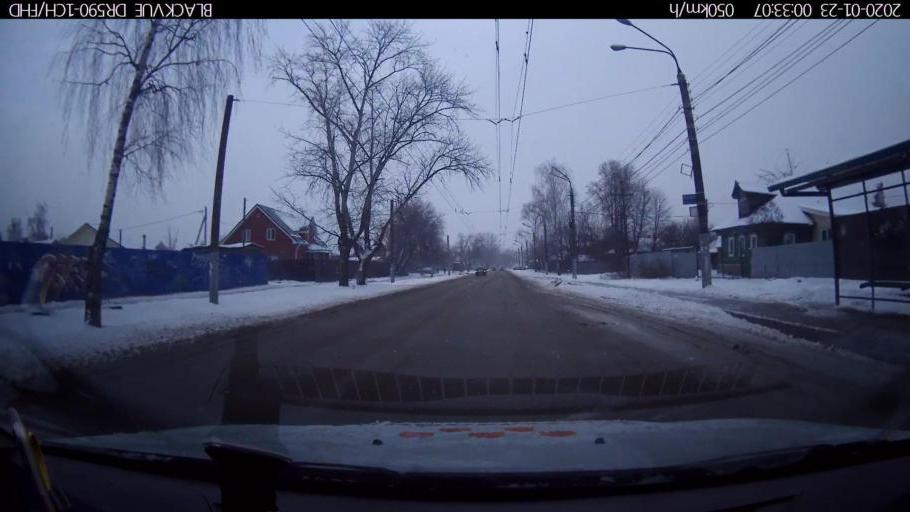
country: RU
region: Nizjnij Novgorod
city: Gorbatovka
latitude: 56.3631
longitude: 43.8371
